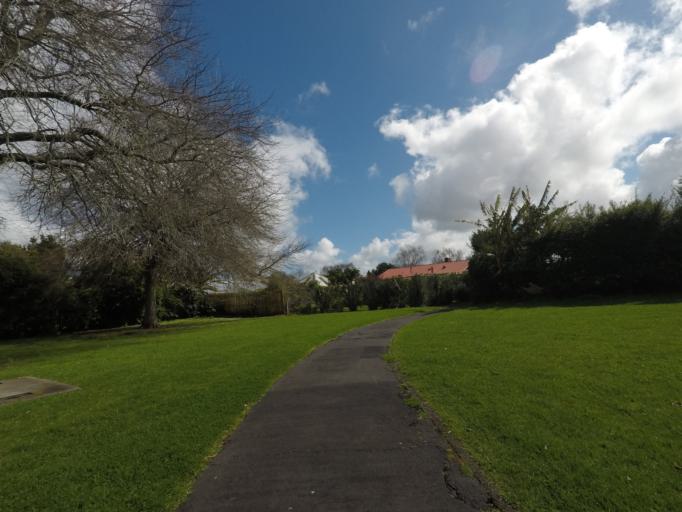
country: NZ
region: Auckland
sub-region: Auckland
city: Rosebank
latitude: -36.8900
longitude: 174.6807
